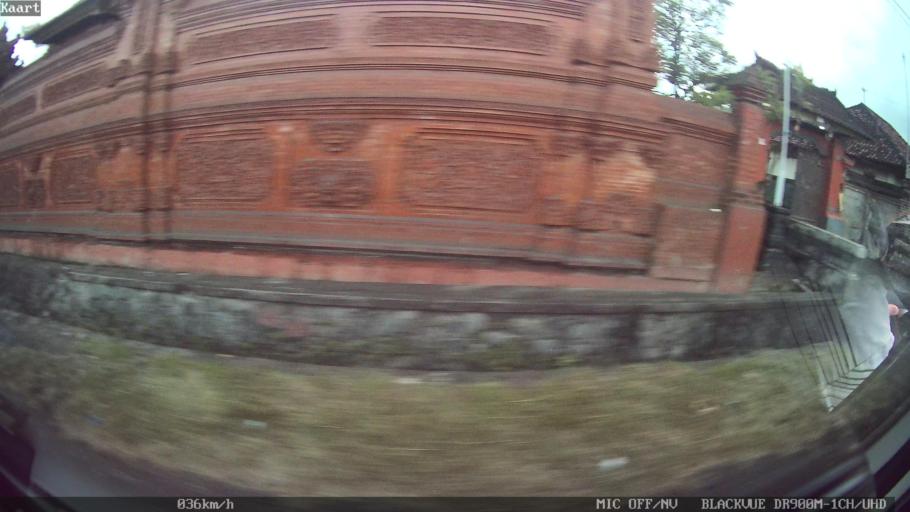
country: ID
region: Bali
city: Banjar Batur
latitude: -8.6005
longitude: 115.2058
